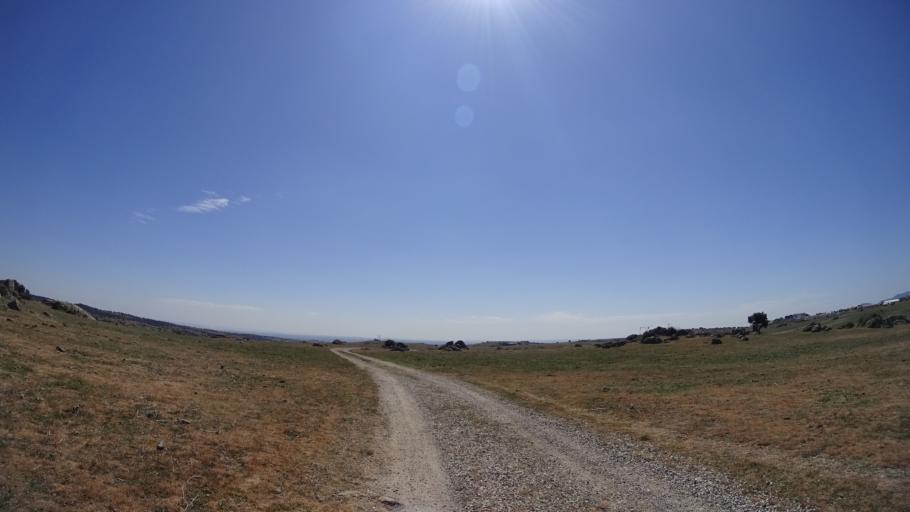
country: ES
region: Madrid
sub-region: Provincia de Madrid
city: Colmenar Viejo
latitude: 40.7033
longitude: -3.7520
